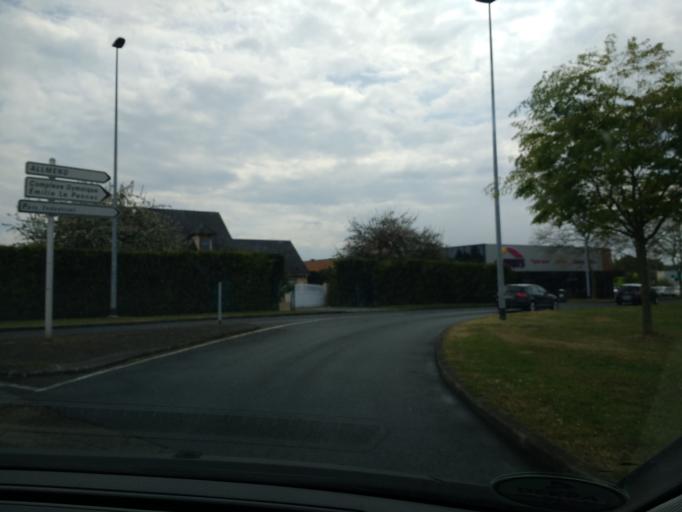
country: FR
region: Lorraine
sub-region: Departement de la Moselle
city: Sarreguemines
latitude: 49.1156
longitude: 7.0945
